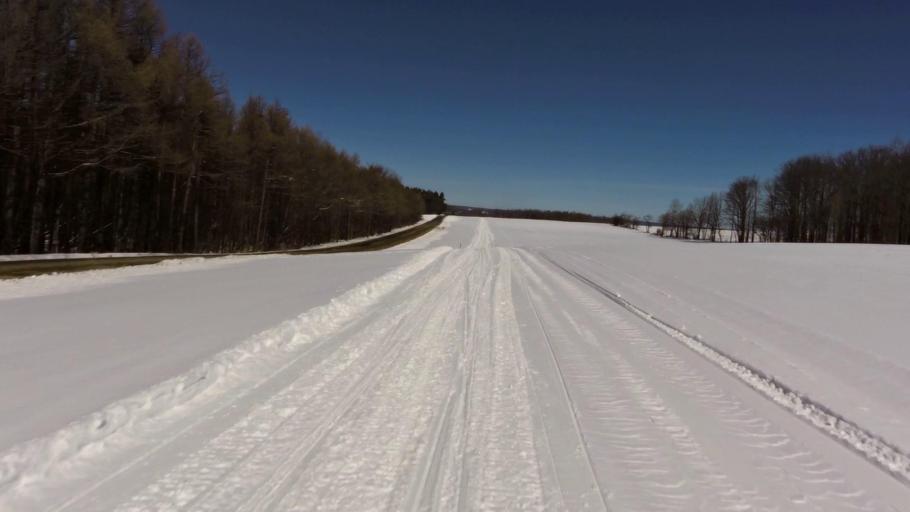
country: US
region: New York
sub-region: Allegany County
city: Houghton
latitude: 42.3521
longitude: -78.2604
